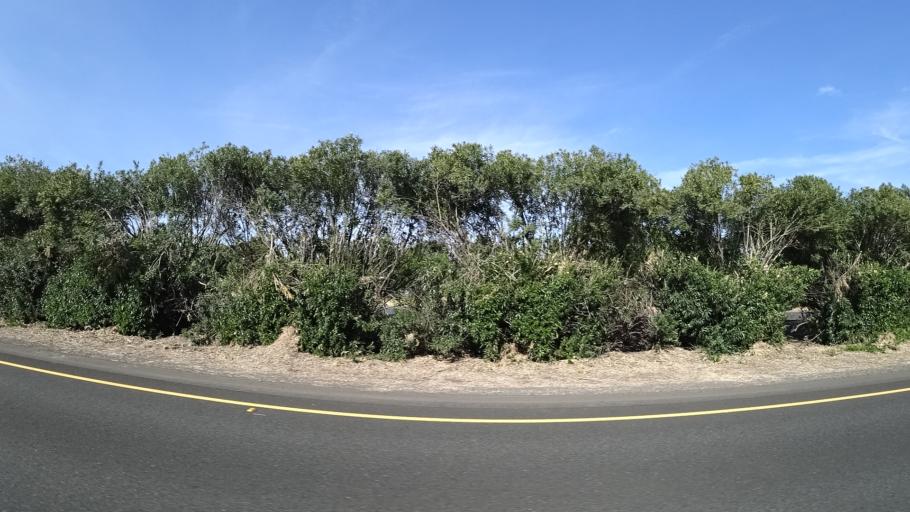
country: US
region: California
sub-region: Butte County
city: Chico
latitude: 39.7706
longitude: -121.8687
